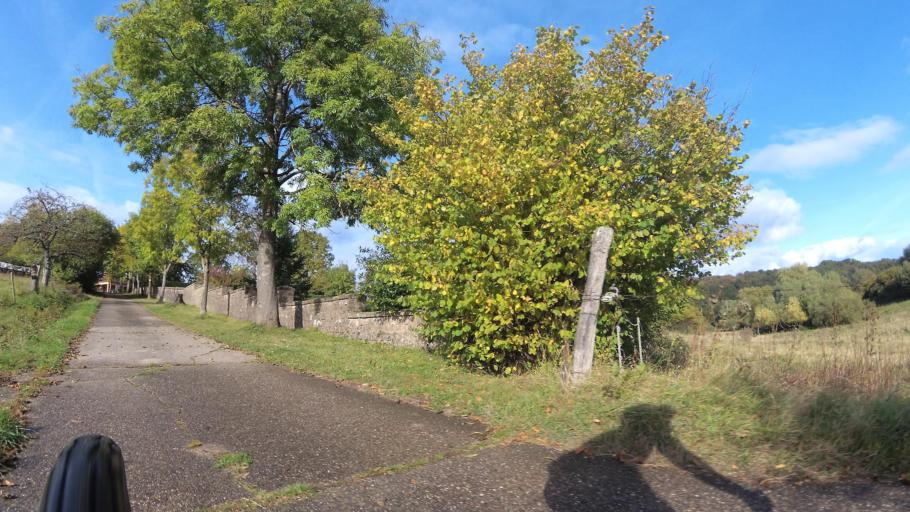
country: DE
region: Rheinland-Pfalz
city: Frohnhofen
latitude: 49.4511
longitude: 7.3065
